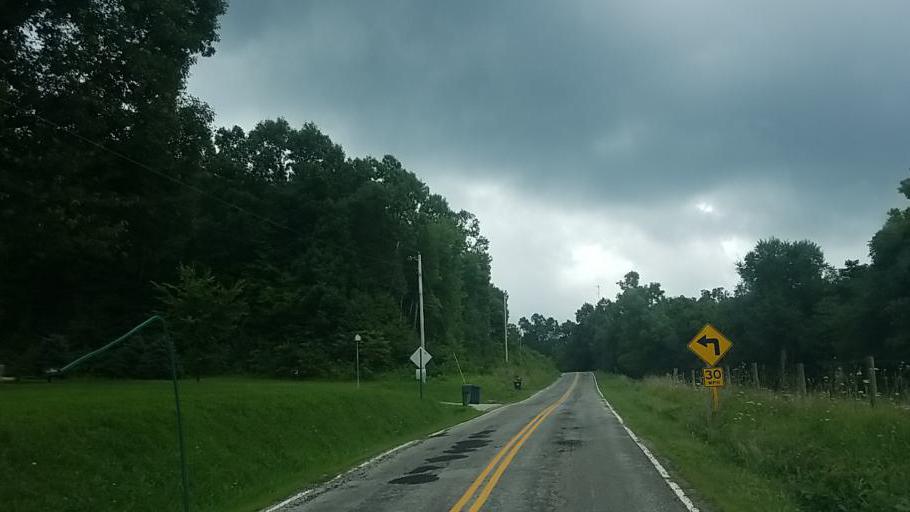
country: US
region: Ohio
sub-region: Muskingum County
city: Frazeysburg
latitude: 40.1724
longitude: -82.2628
